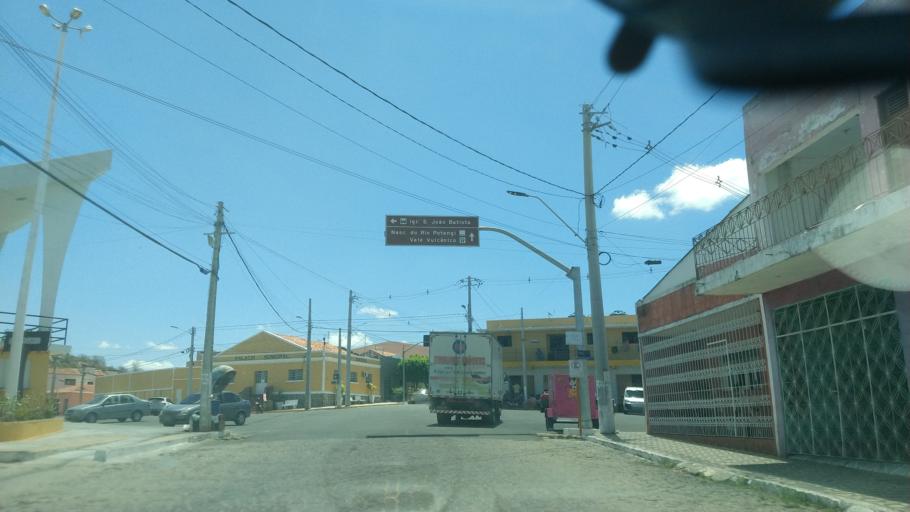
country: BR
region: Rio Grande do Norte
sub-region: Cerro Cora
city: Cerro Cora
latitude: -6.0450
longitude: -36.3465
